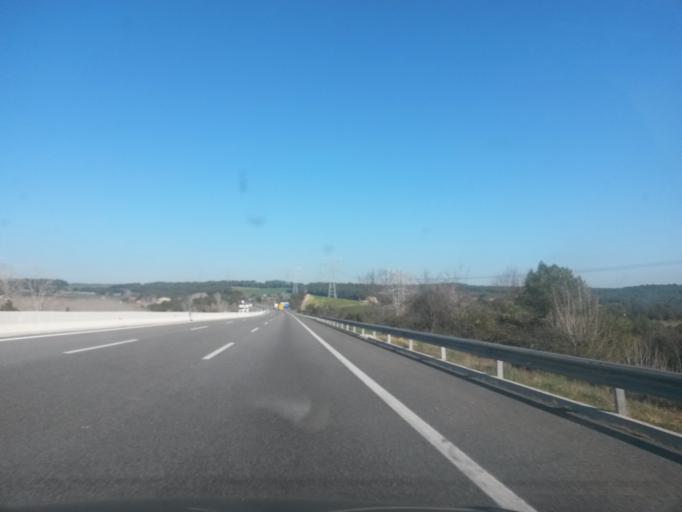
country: ES
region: Catalonia
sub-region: Provincia de Girona
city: Cervia de Ter
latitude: 42.1010
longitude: 2.9029
